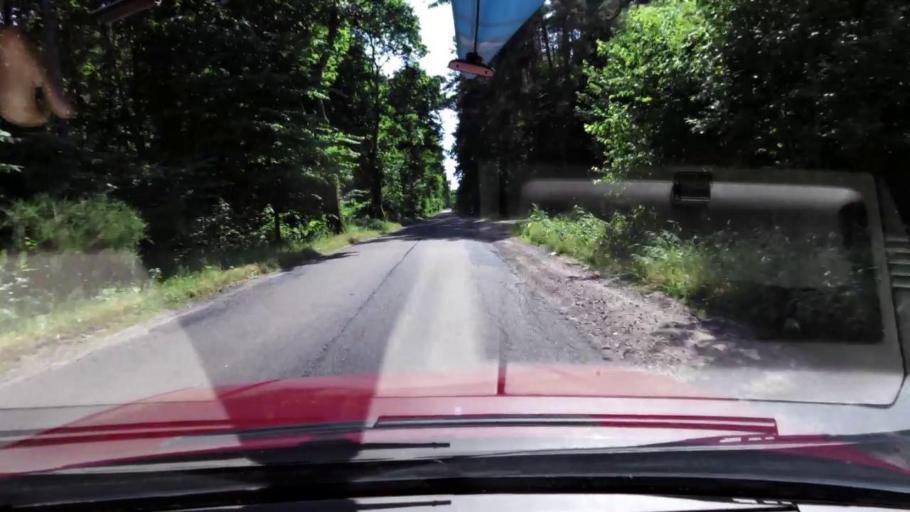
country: PL
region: Pomeranian Voivodeship
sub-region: Powiat slupski
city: Kobylnica
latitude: 54.3429
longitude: 16.9644
